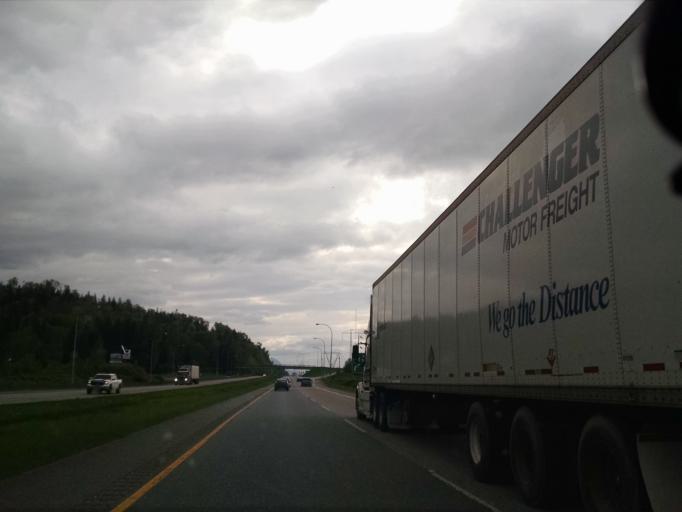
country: CA
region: British Columbia
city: Agassiz
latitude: 49.1835
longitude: -121.7555
